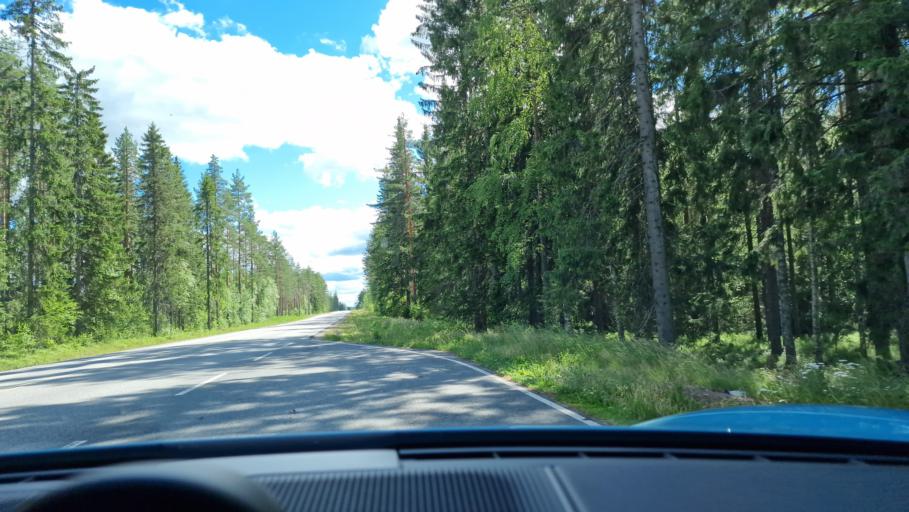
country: FI
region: Central Finland
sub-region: Saarijaervi-Viitasaari
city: Pylkoenmaeki
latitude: 62.6436
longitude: 24.5755
